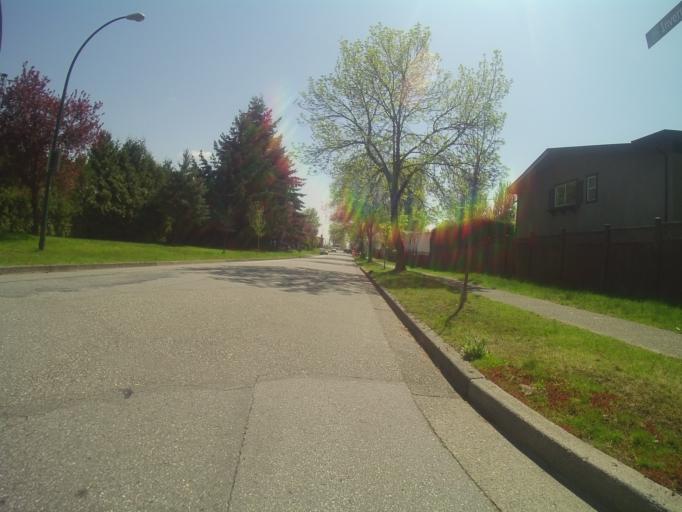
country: CA
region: British Columbia
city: Vancouver
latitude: 49.2269
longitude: -123.0801
